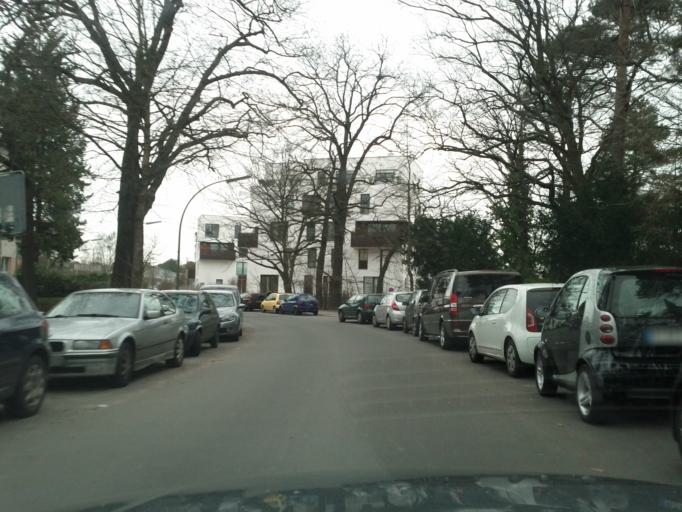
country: DE
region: Berlin
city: Dahlem
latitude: 52.4513
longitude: 13.2685
